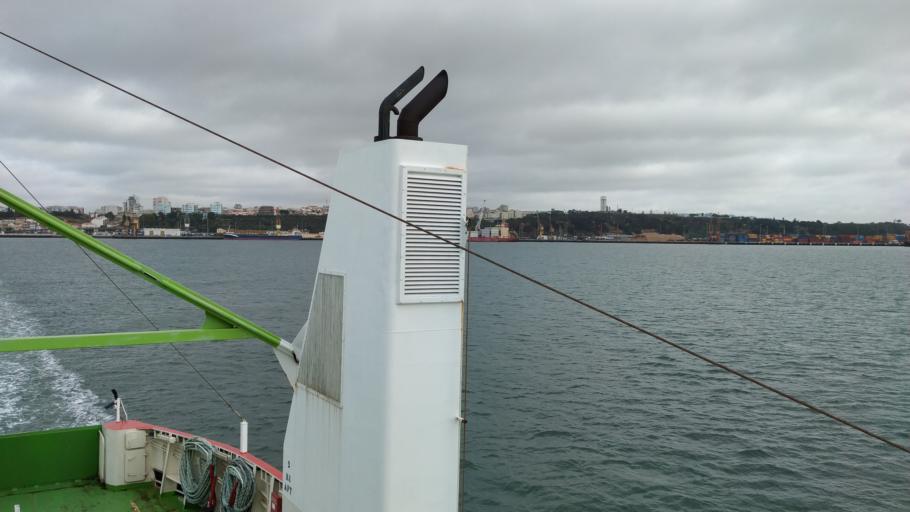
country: PT
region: Setubal
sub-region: Setubal
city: Setubal
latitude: 38.5112
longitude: -8.8867
